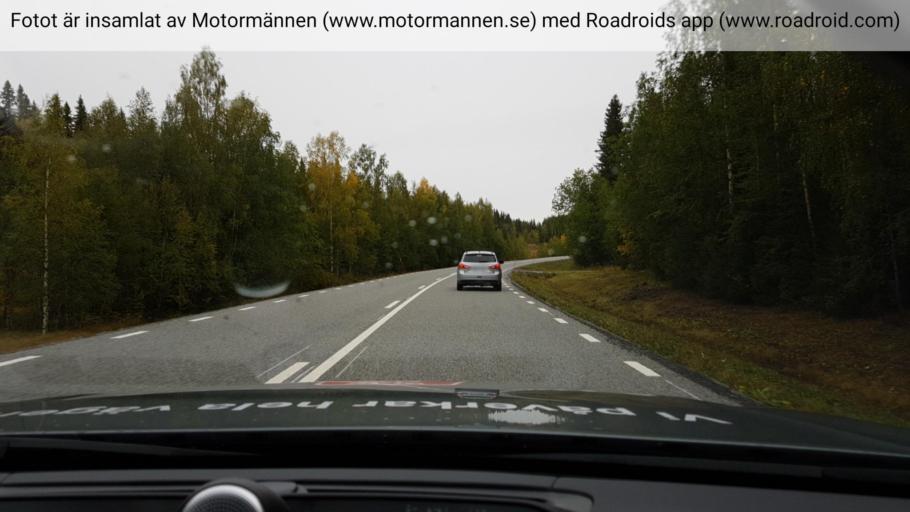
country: SE
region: Jaemtland
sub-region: Stroemsunds Kommun
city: Stroemsund
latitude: 64.0669
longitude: 15.5555
